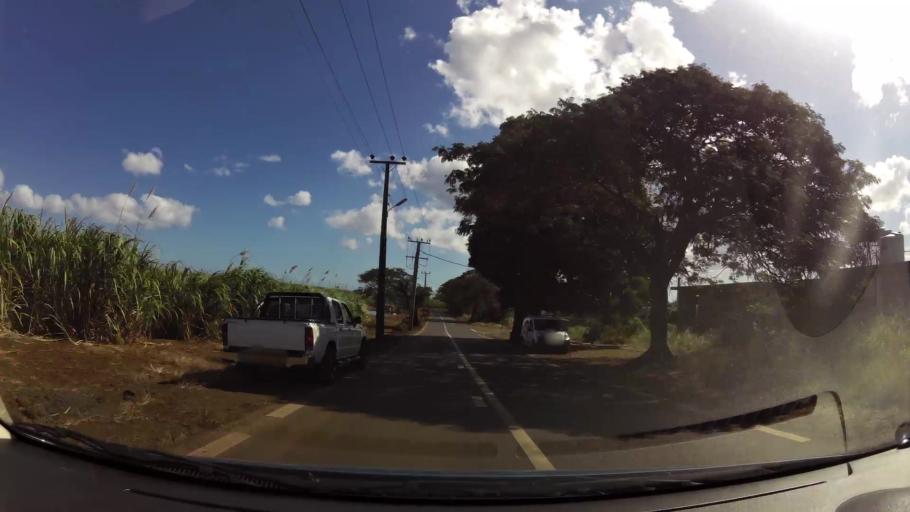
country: MU
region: Black River
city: Gros Cailloux
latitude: -20.2224
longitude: 57.4279
